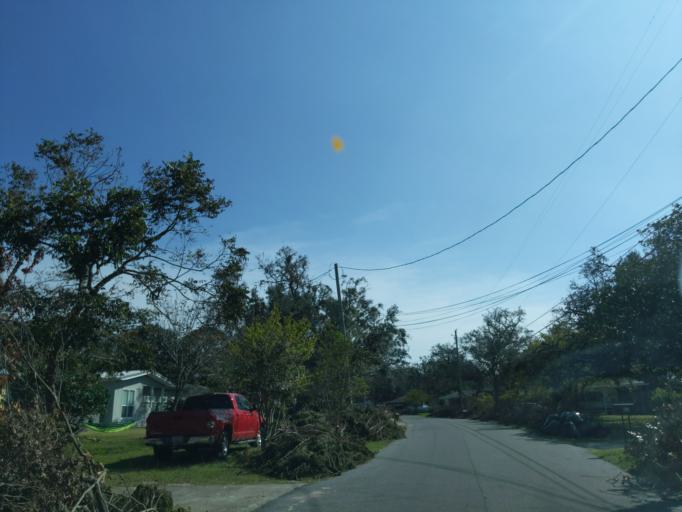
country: US
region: Florida
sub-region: Santa Rosa County
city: Gulf Breeze
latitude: 30.3583
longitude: -87.1928
